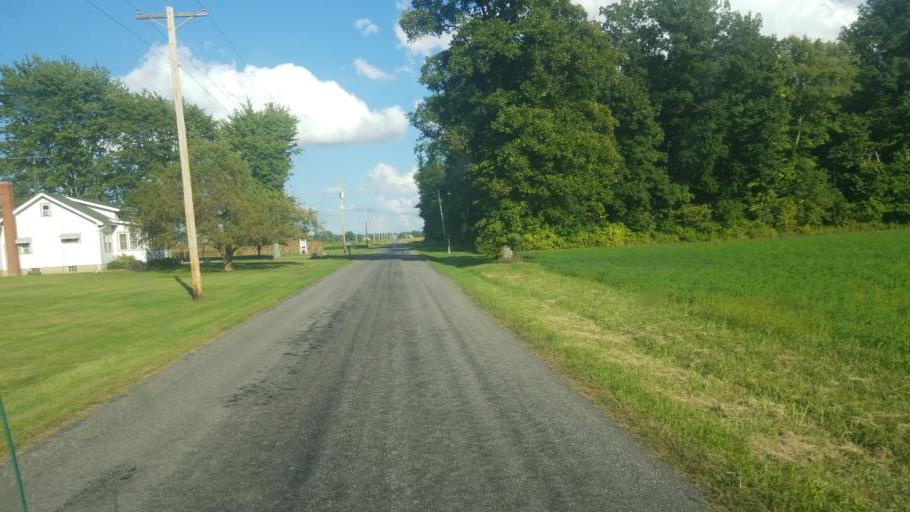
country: US
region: Ohio
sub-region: Hancock County
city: Arlington
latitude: 40.9362
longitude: -83.7126
